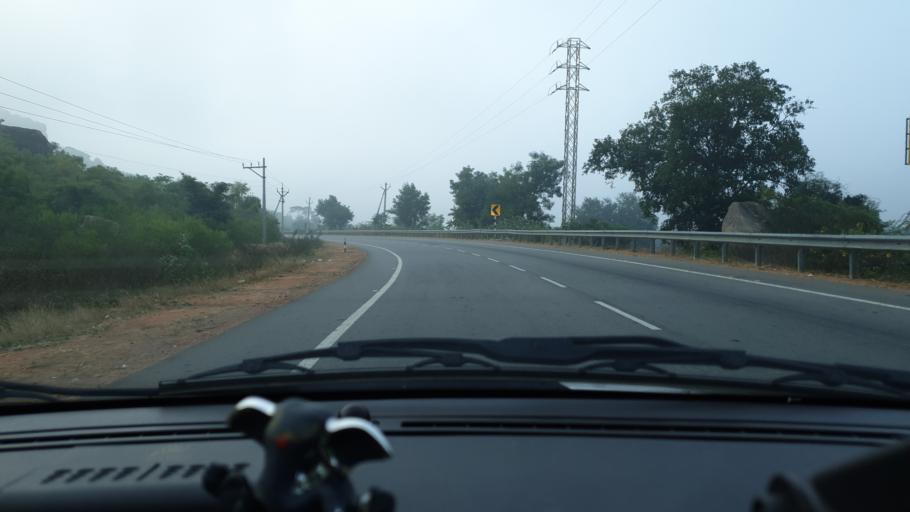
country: IN
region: Telangana
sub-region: Mahbubnagar
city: Farrukhnagar
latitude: 16.8951
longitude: 78.5297
